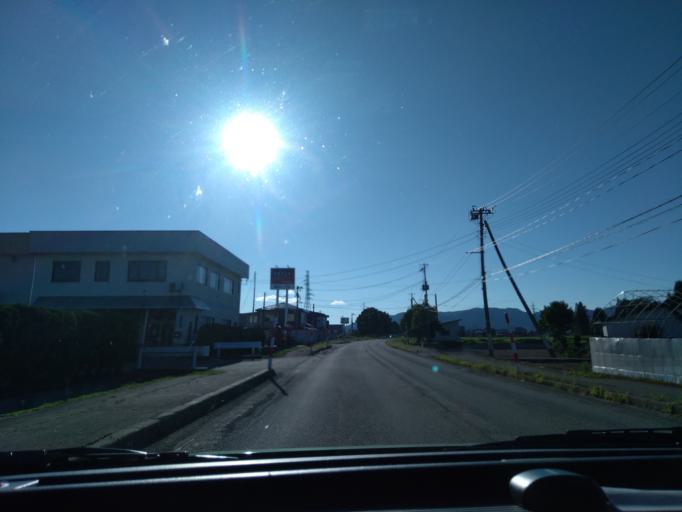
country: JP
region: Akita
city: Omagari
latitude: 39.4245
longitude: 140.4988
